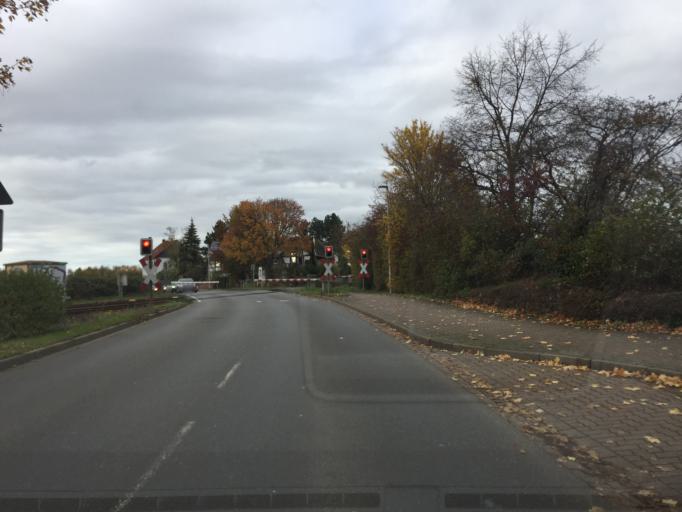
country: DE
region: Lower Saxony
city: Wolfenbuettel
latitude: 52.1743
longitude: 10.5153
